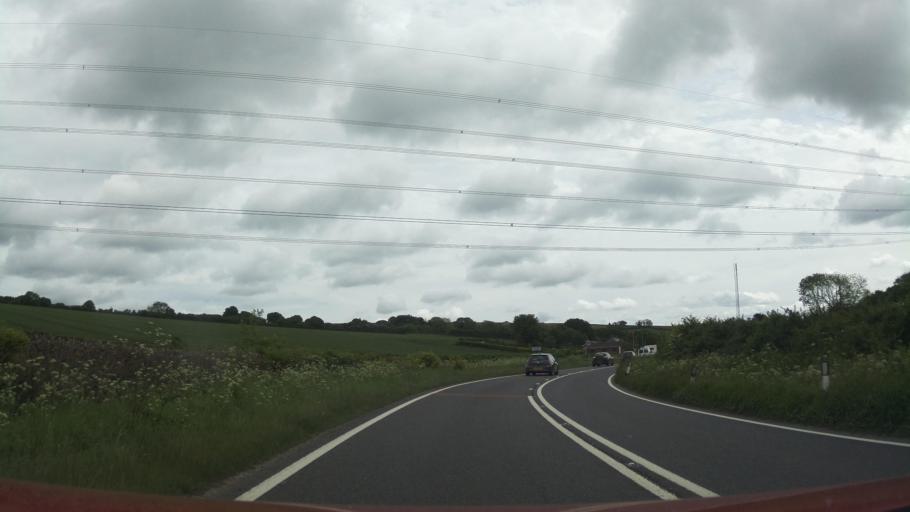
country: GB
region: England
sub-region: Dorset
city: Chickerell
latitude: 50.7132
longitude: -2.5508
